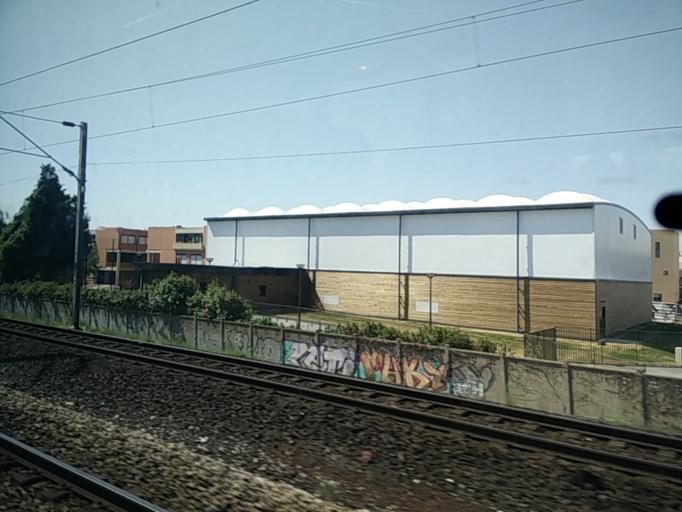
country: FR
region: Ile-de-France
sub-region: Departement de Seine-Saint-Denis
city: Villemomble
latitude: 48.8812
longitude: 2.4824
